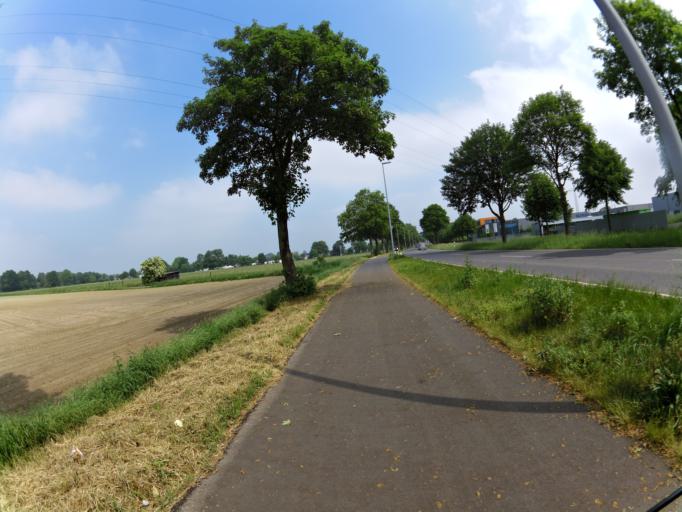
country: DE
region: North Rhine-Westphalia
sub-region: Regierungsbezirk Koln
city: Wassenberg
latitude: 51.0507
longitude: 6.1543
